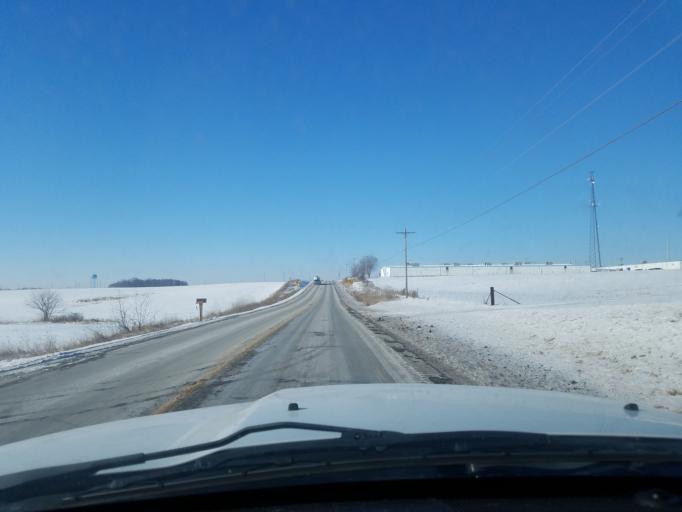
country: US
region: Indiana
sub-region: Noble County
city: Albion
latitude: 41.3959
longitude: -85.3904
